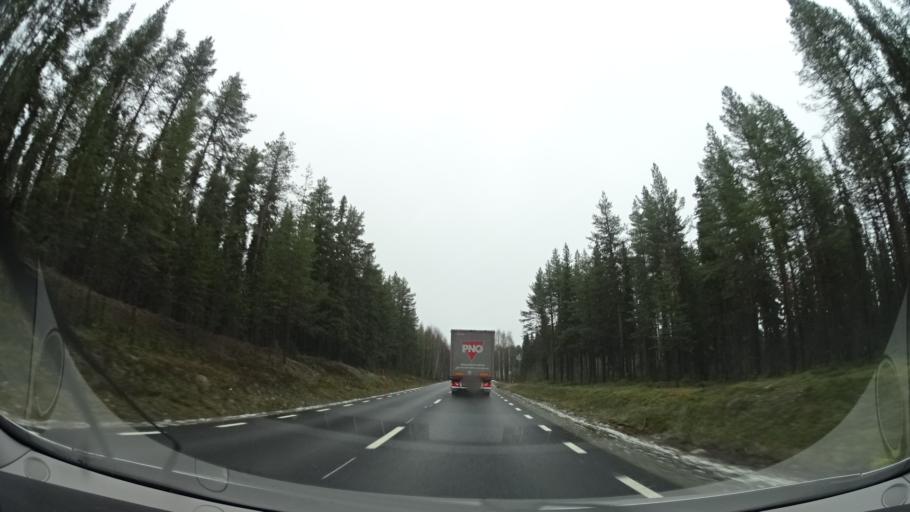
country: SE
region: Vaesterbotten
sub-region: Dorotea Kommun
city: Dorotea
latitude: 64.2409
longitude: 16.3163
